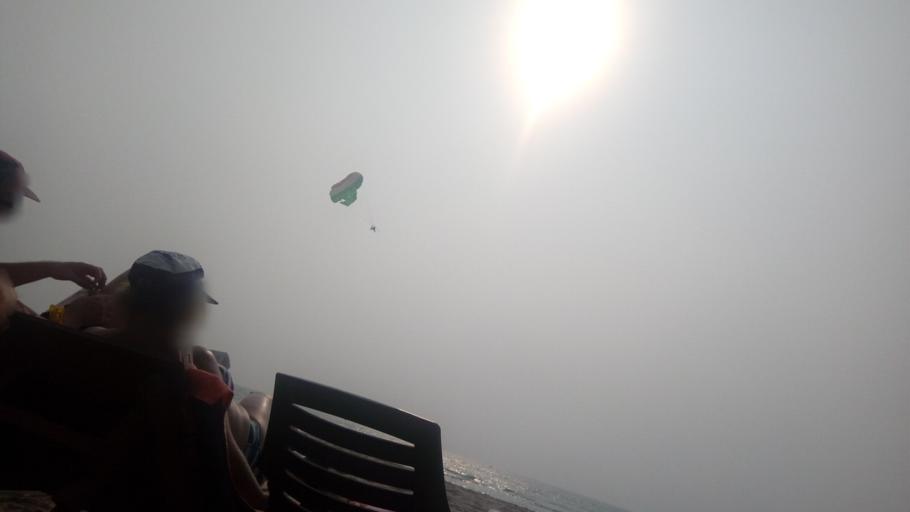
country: IN
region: Goa
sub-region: South Goa
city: Benaulim
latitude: 15.2586
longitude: 73.9185
